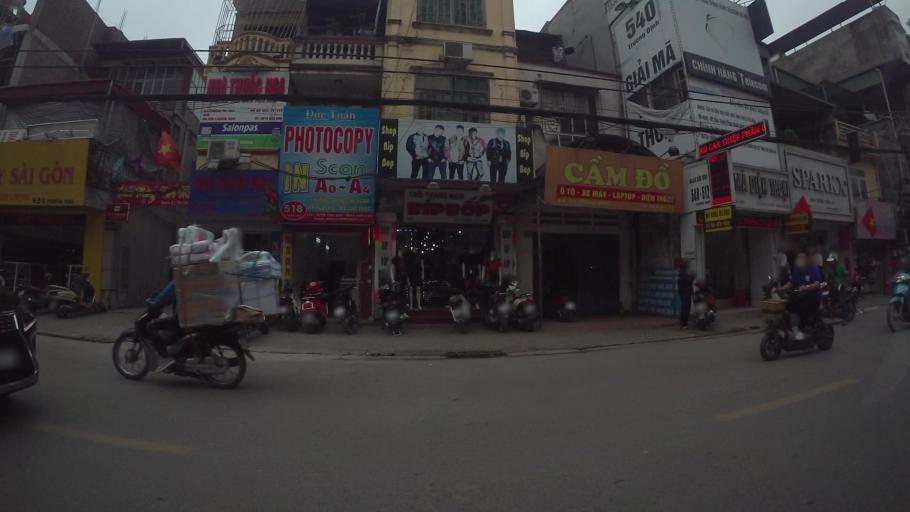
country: VN
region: Ha Noi
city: Hai BaTrung
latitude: 20.9844
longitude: 105.8462
